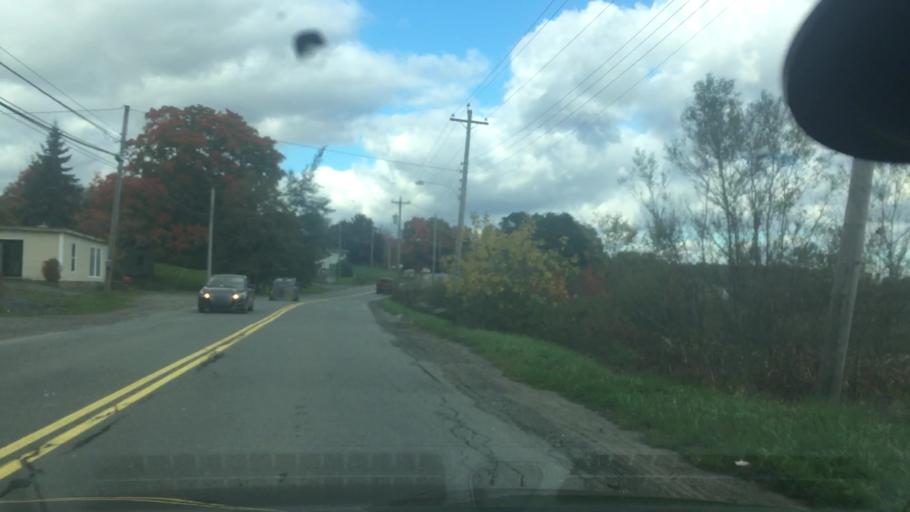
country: CA
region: Nova Scotia
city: Windsor
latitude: 44.9766
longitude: -64.1206
